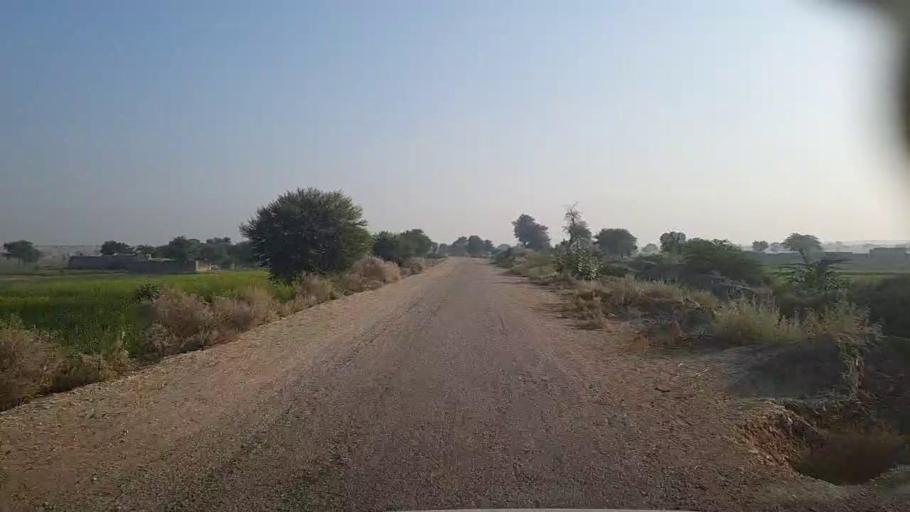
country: PK
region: Sindh
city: Karaundi
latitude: 26.7302
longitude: 68.4860
